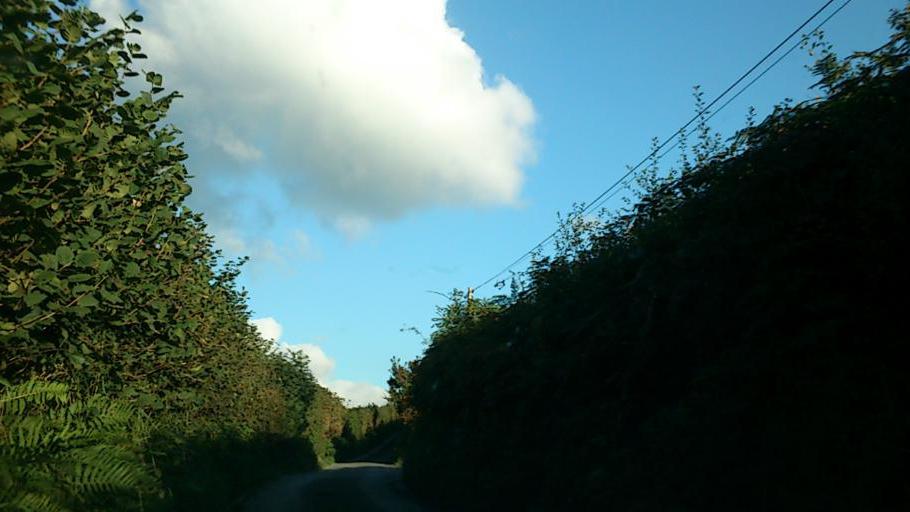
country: GB
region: Wales
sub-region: County of Ceredigion
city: Bow Street
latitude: 52.4570
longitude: -4.0045
